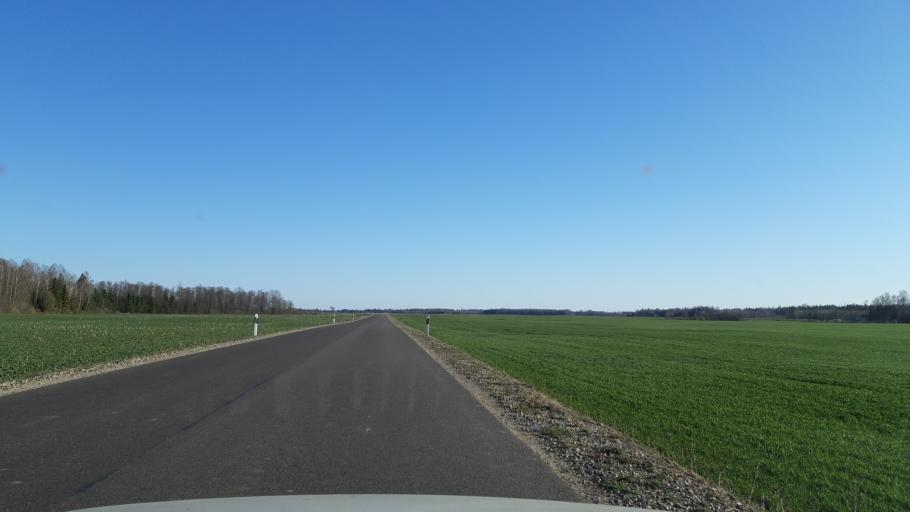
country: LT
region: Kauno apskritis
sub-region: Kaunas
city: Sargenai
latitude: 55.0267
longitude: 23.7607
